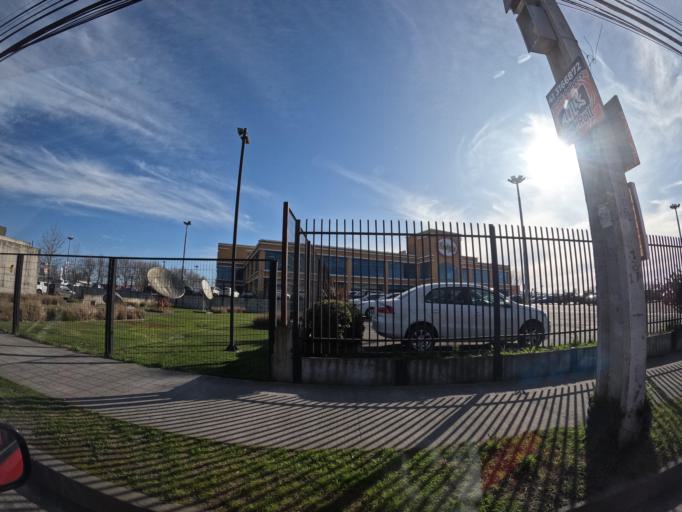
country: CL
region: Biobio
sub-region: Provincia de Concepcion
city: Concepcion
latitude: -36.7776
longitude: -73.0759
